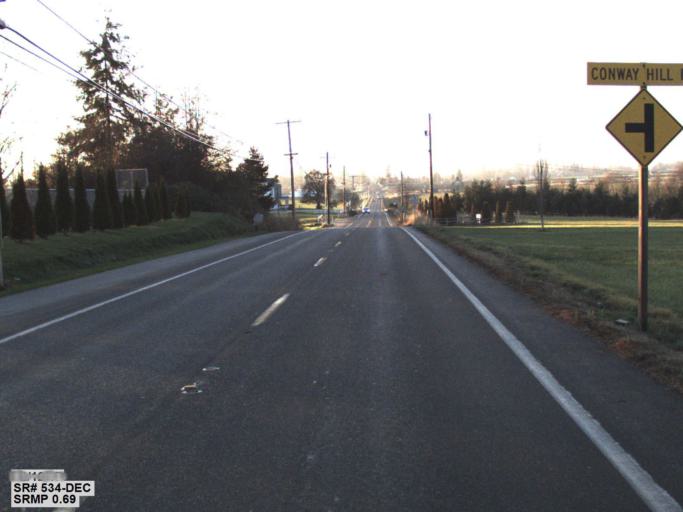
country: US
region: Washington
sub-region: Skagit County
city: Mount Vernon
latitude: 48.3409
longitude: -122.3199
